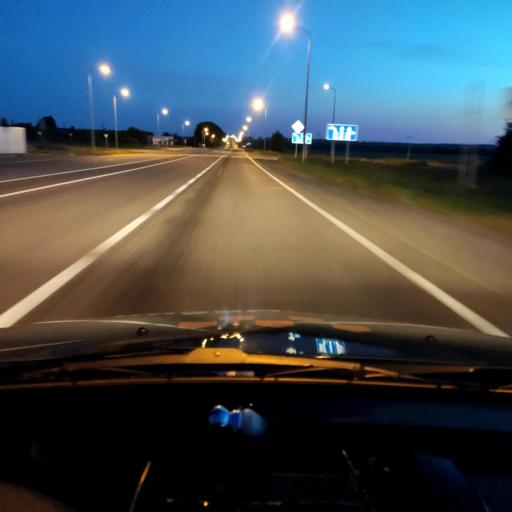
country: RU
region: Belgorod
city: Skorodnoye
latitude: 51.1842
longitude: 37.3578
